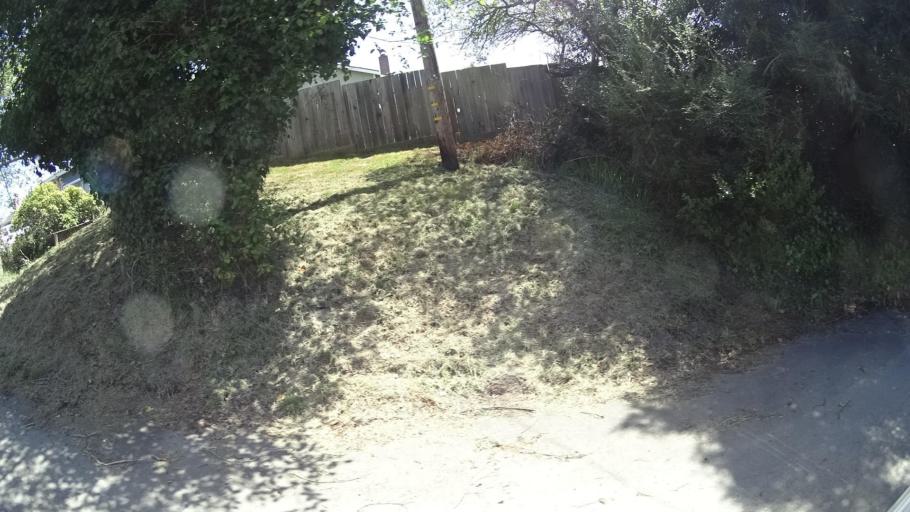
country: US
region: California
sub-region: Humboldt County
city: Bayview
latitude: 40.7739
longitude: -124.1716
